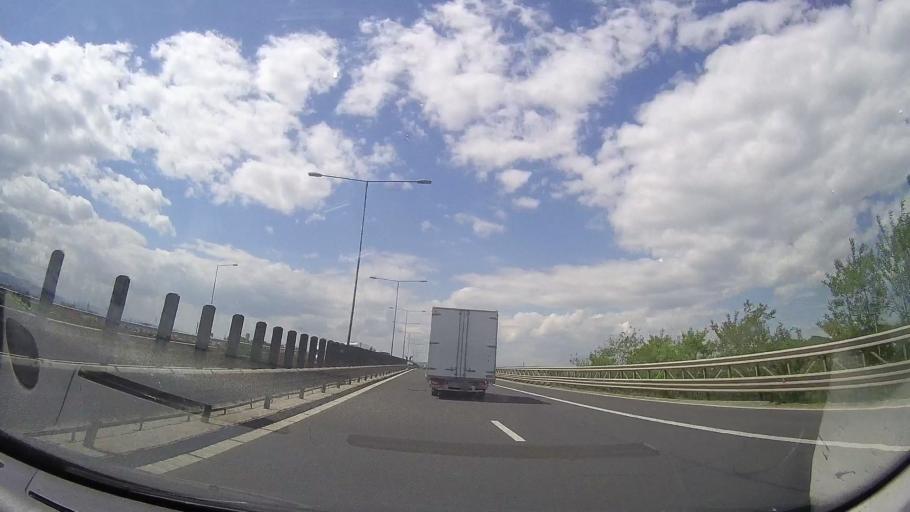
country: RO
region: Sibiu
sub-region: Municipiul Sibiu
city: Sibiu
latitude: 45.8016
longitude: 24.1865
